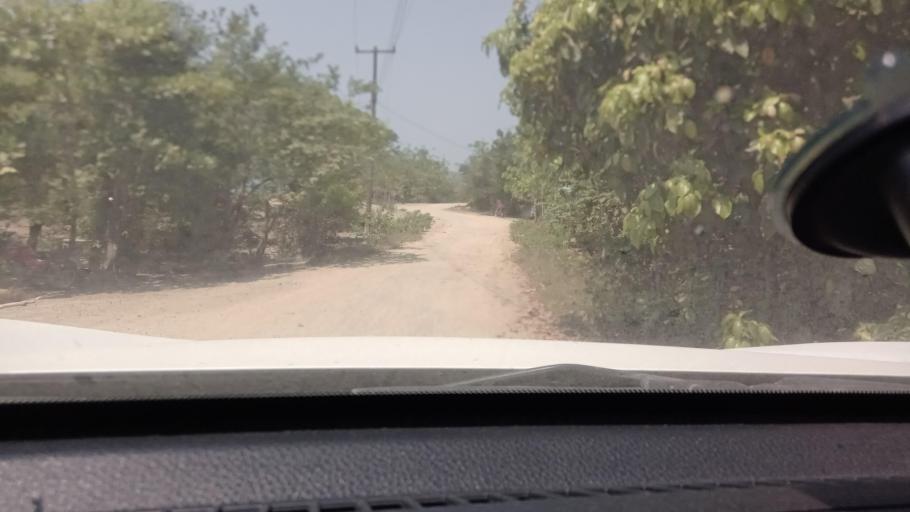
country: MX
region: Tabasco
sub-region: Huimanguillo
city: Francisco Rueda
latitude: 17.4987
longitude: -93.9055
